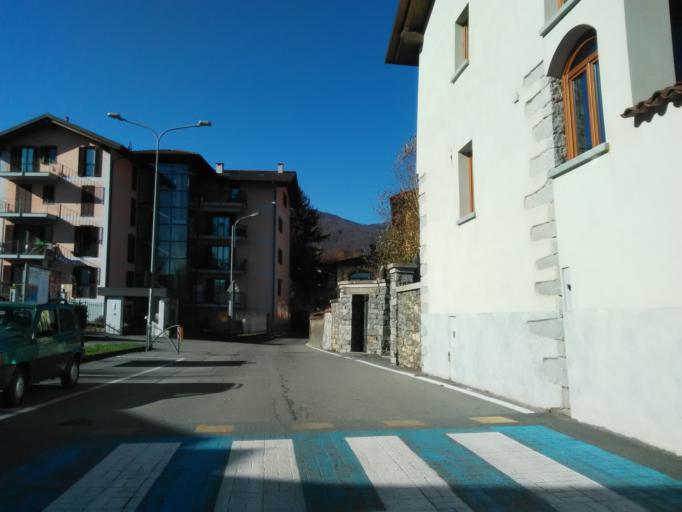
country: IT
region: Piedmont
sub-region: Provincia di Vercelli
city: Borgosesia
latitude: 45.7350
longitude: 8.2749
